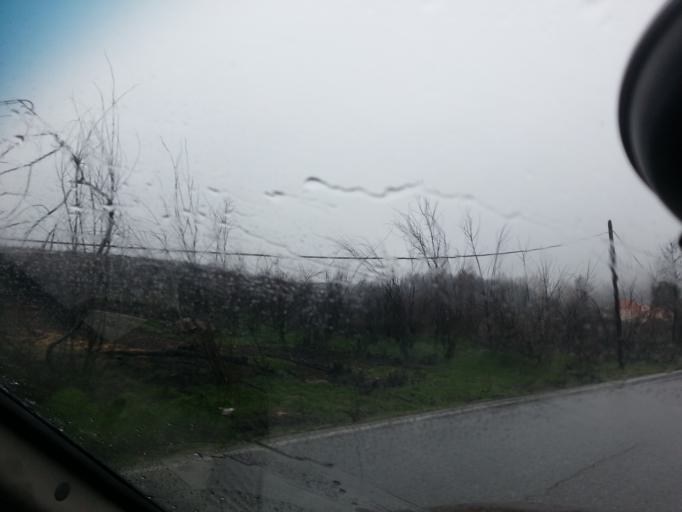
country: PT
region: Viseu
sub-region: Mangualde
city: Mangualde
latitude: 40.6067
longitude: -7.7113
